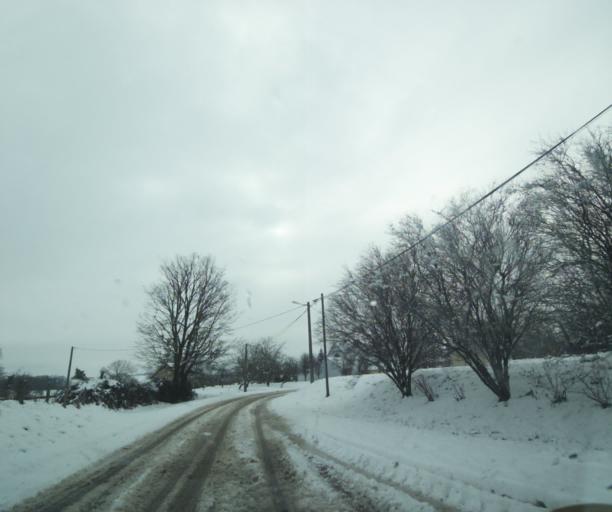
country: FR
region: Champagne-Ardenne
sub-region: Departement de la Haute-Marne
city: Montier-en-Der
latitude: 48.5191
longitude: 4.7007
